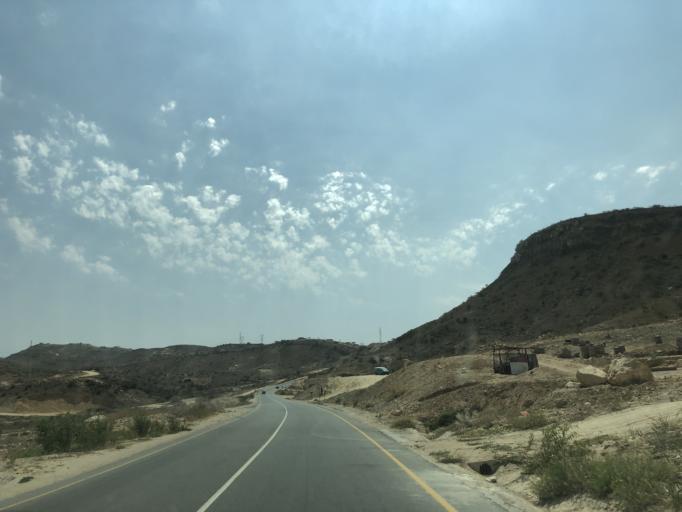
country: AO
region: Benguela
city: Catumbela
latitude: -12.4018
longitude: 13.6284
